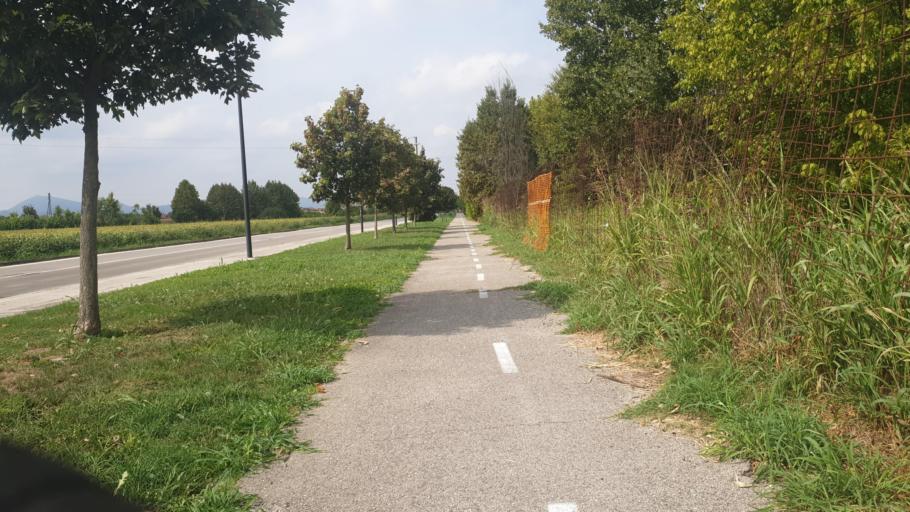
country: IT
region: Veneto
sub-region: Provincia di Padova
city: Albignasego
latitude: 45.3369
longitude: 11.8791
